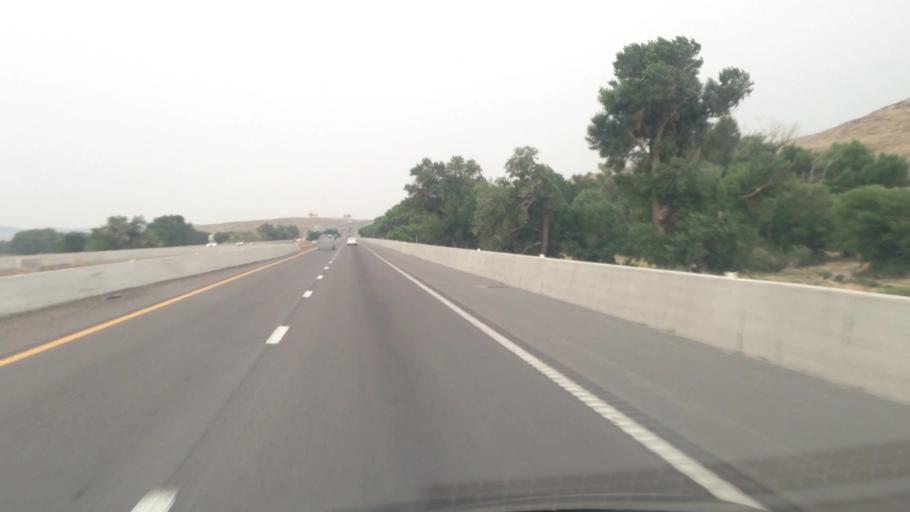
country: US
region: Nevada
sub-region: Lyon County
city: Fernley
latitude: 39.6170
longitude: -119.3018
